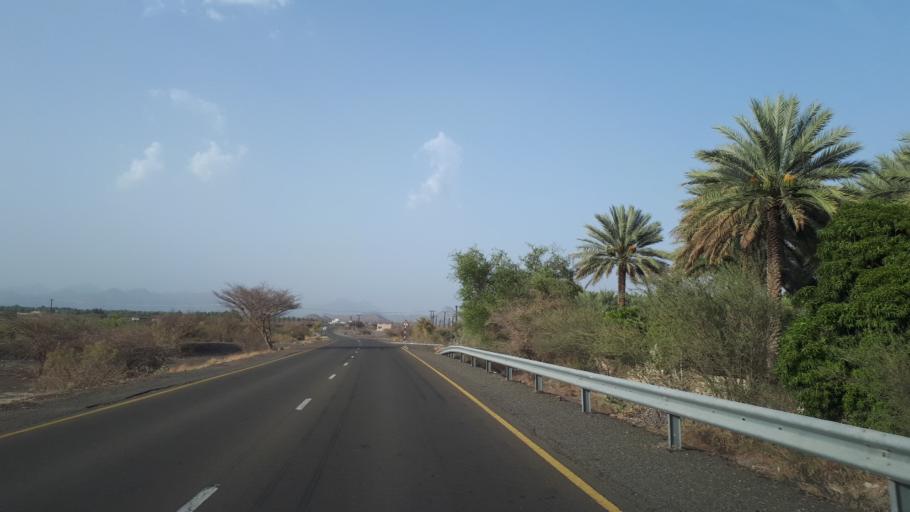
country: OM
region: Az Zahirah
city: Yanqul
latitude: 23.4163
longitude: 56.7472
